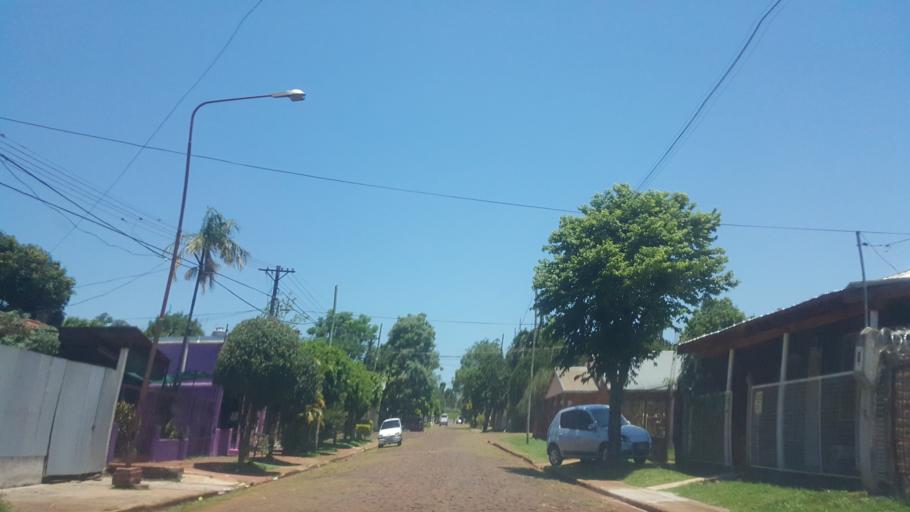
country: AR
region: Misiones
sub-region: Departamento de Capital
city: Posadas
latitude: -27.3764
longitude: -55.9150
